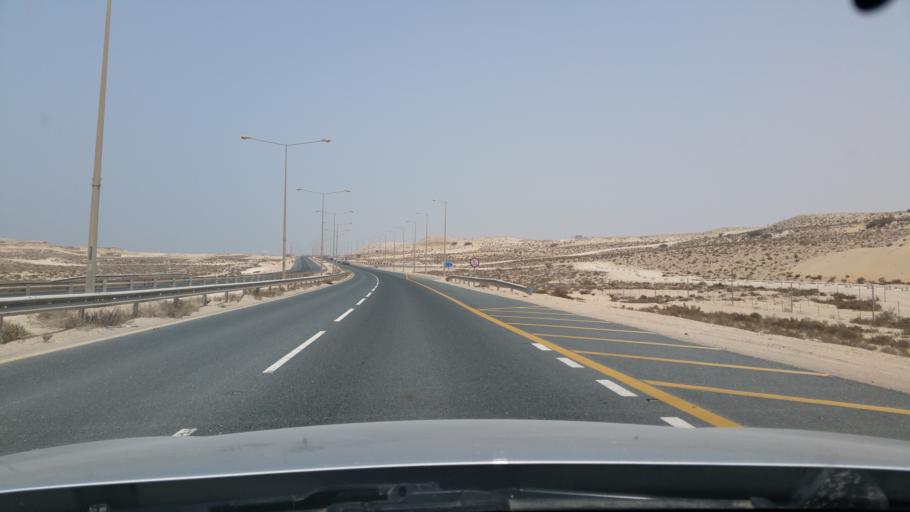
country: QA
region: Baladiyat ar Rayyan
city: Dukhan
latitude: 25.3467
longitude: 50.7826
